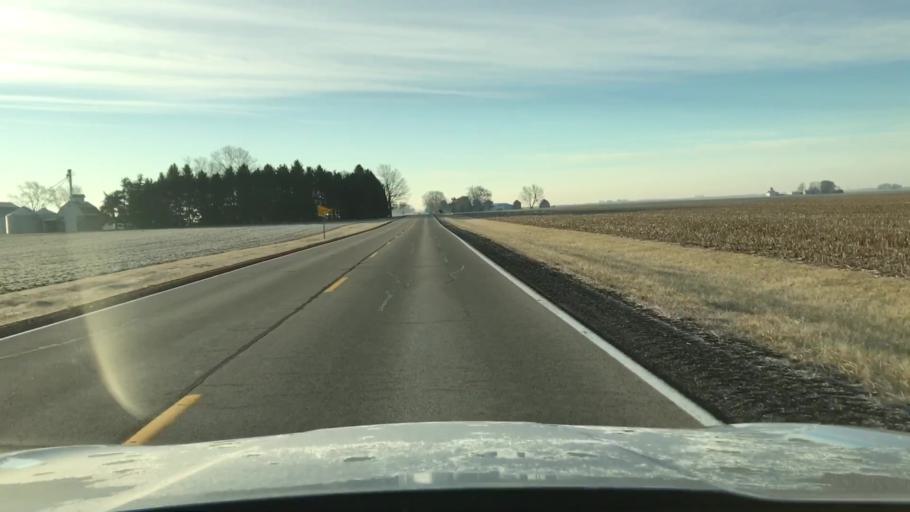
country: US
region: Illinois
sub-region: McLean County
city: Hudson
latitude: 40.6162
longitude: -88.9455
